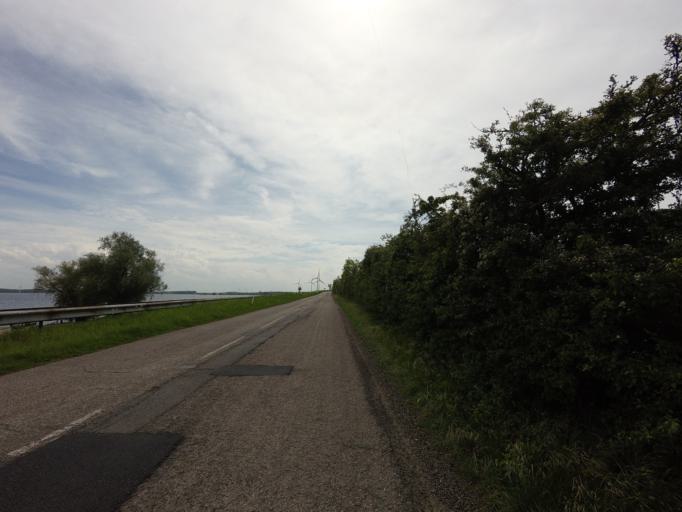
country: NL
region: North Brabant
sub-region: Gemeente Moerdijk
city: Willemstad
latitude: 51.7231
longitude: 4.4056
